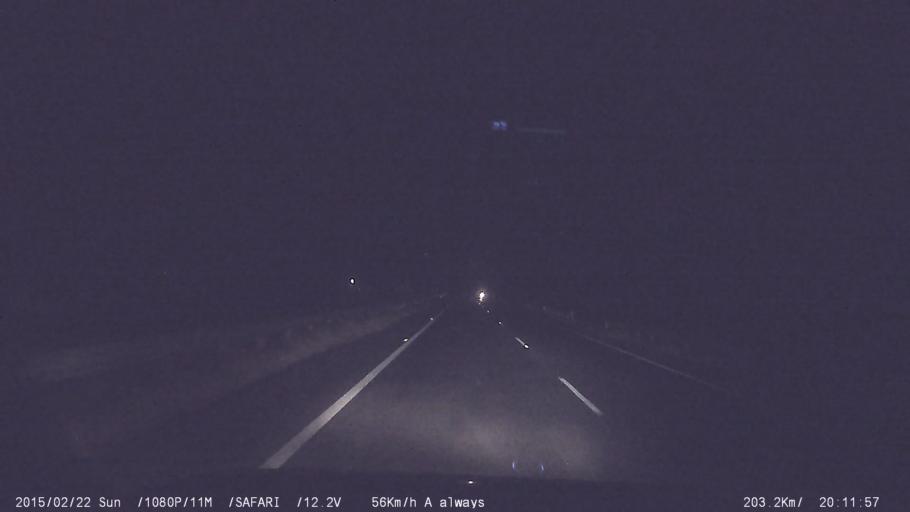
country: IN
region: Tamil Nadu
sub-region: Dindigul
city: Nilakottai
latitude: 10.2340
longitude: 77.8168
